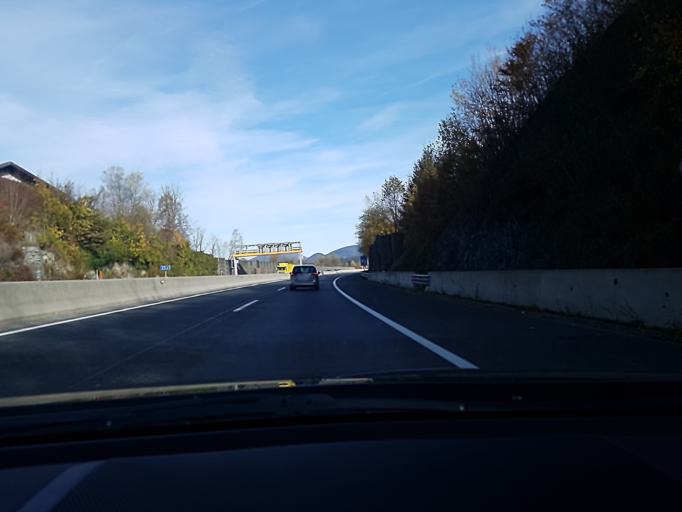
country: AT
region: Salzburg
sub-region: Politischer Bezirk Hallein
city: Kuchl
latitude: 47.6316
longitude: 13.1318
